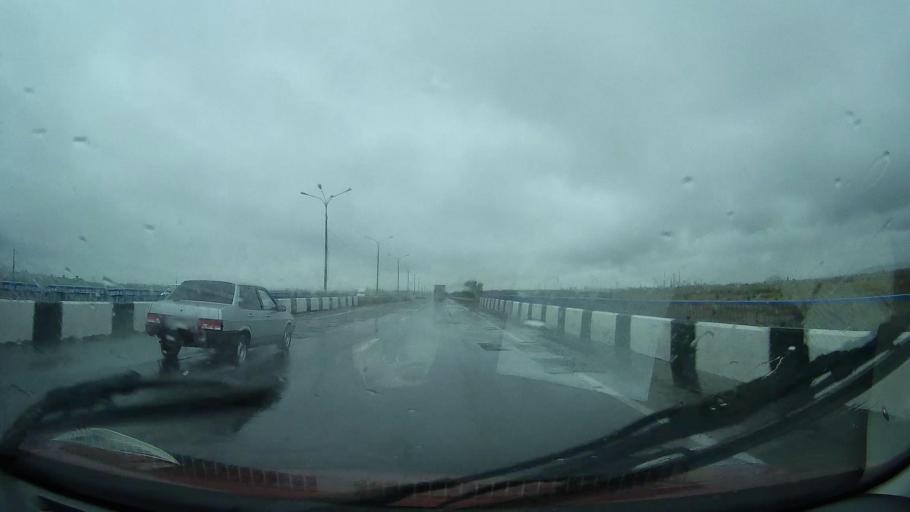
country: RU
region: Stavropol'skiy
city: Nevinnomyssk
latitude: 44.6368
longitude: 41.9927
